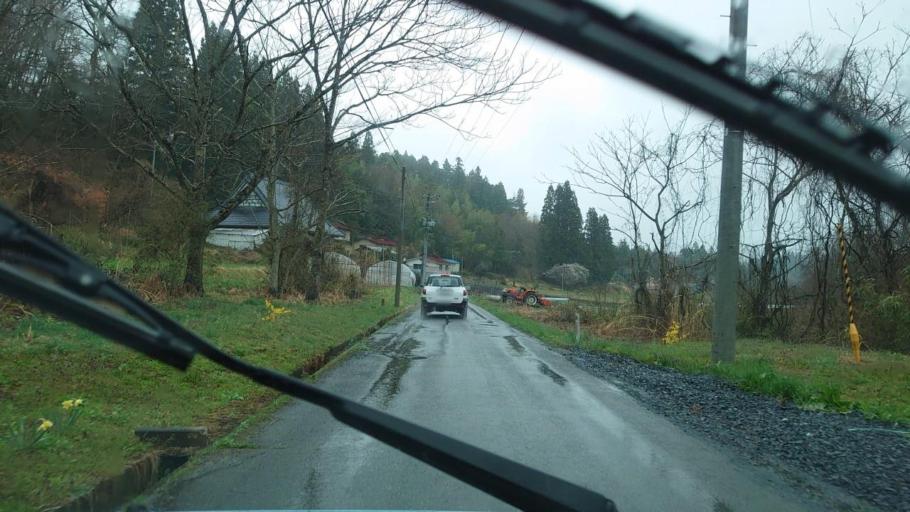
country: JP
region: Iwate
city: Ichinoseki
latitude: 38.8313
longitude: 141.3513
